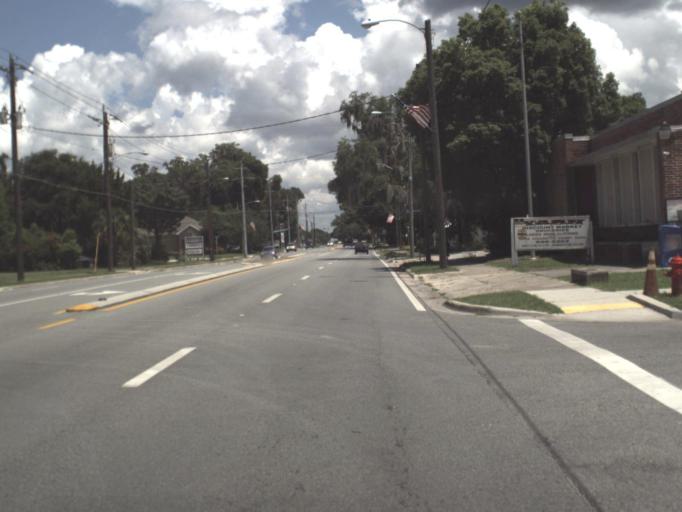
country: US
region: Florida
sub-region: Putnam County
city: Crescent City
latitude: 29.4338
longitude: -81.5104
